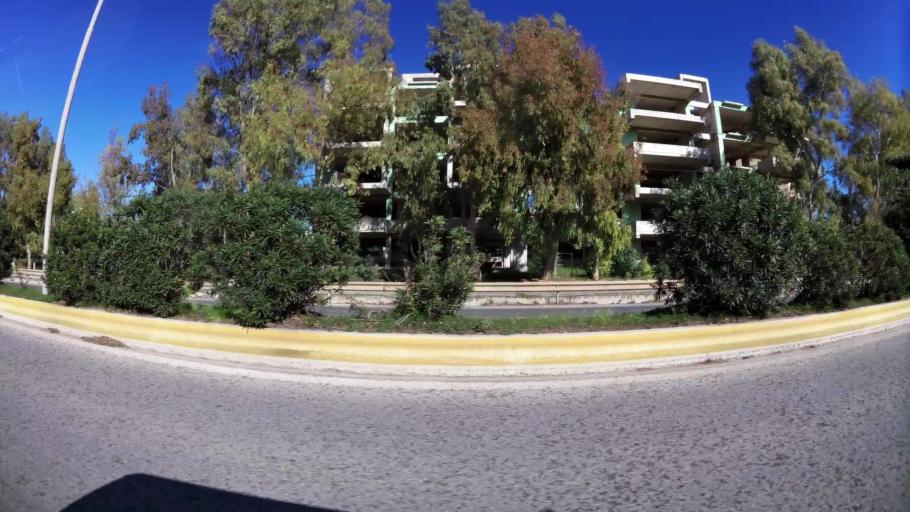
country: GR
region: Attica
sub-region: Nomarchia Anatolikis Attikis
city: Markopoulo
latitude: 37.8770
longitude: 23.9293
